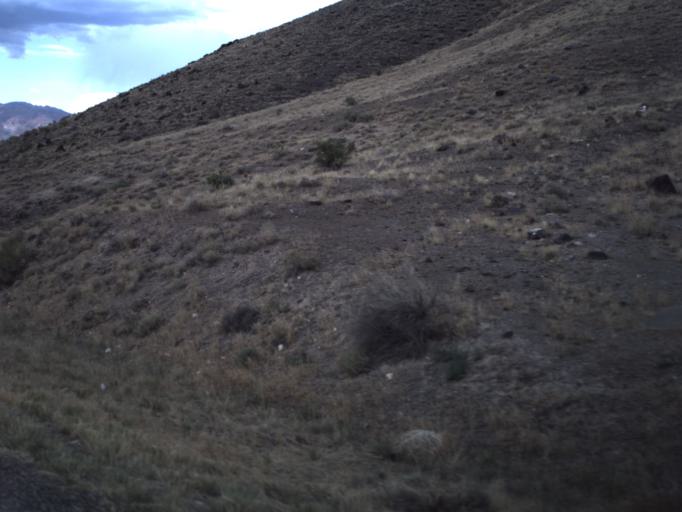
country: US
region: Utah
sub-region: Sevier County
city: Richfield
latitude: 38.7721
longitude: -111.9835
